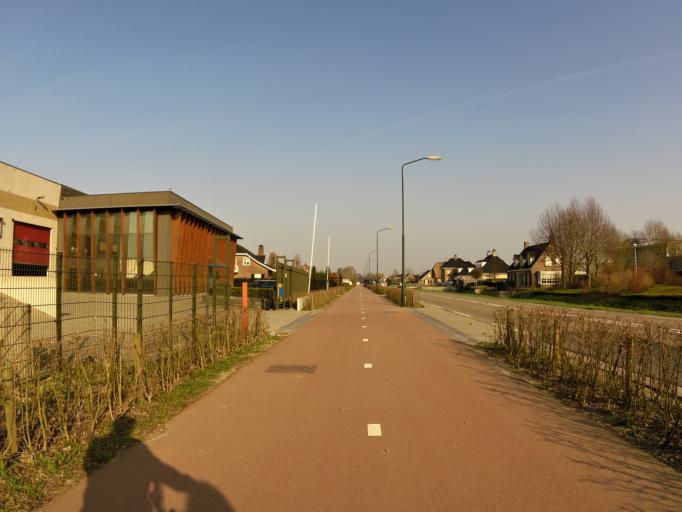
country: NL
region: North Brabant
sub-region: Gemeente Aalburg
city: Aalburg
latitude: 51.7737
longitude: 5.0923
